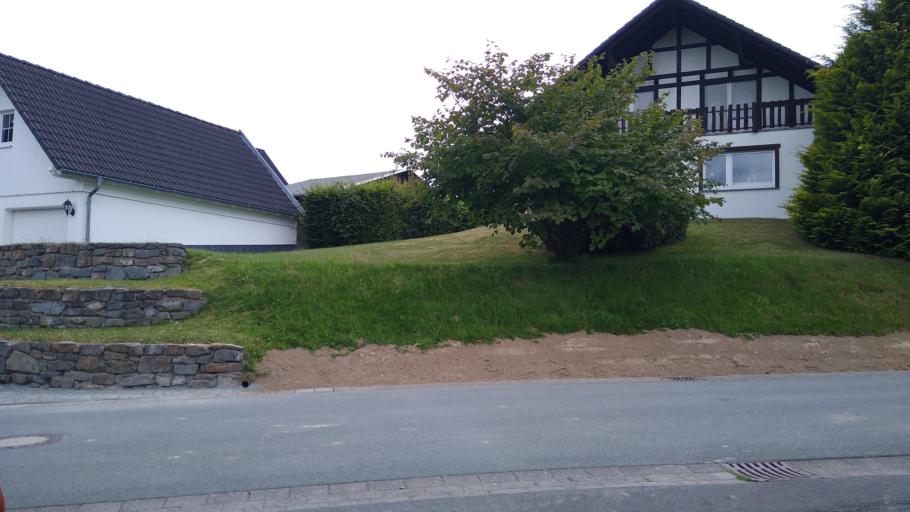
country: DE
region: North Rhine-Westphalia
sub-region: Regierungsbezirk Arnsberg
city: Schmallenberg
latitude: 51.1669
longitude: 8.2117
